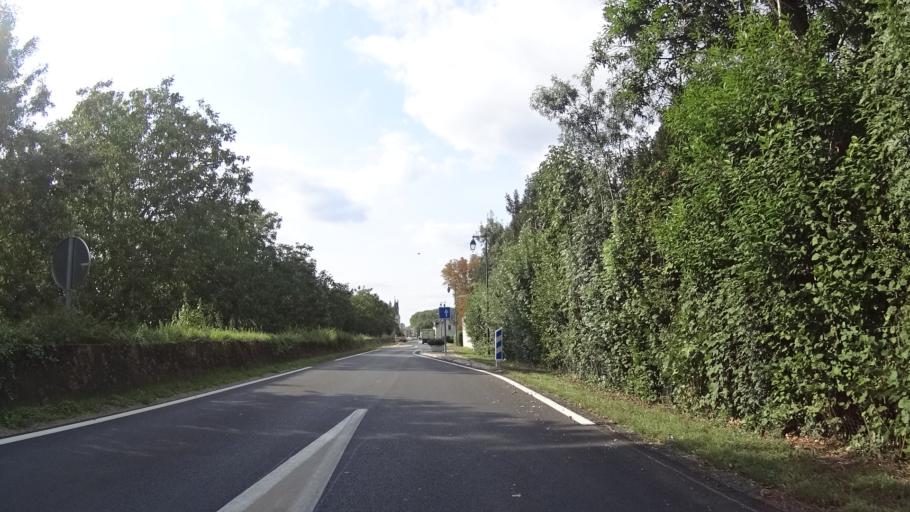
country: FR
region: Pays de la Loire
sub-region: Departement de Maine-et-Loire
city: Chenehutte-Treves-Cunault
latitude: 47.3193
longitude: -0.1575
